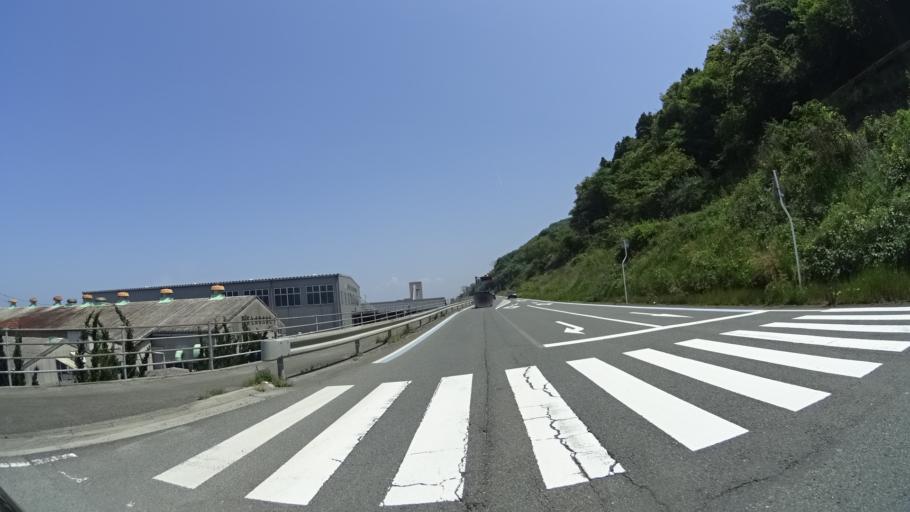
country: JP
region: Ehime
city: Ozu
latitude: 33.6229
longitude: 132.5022
